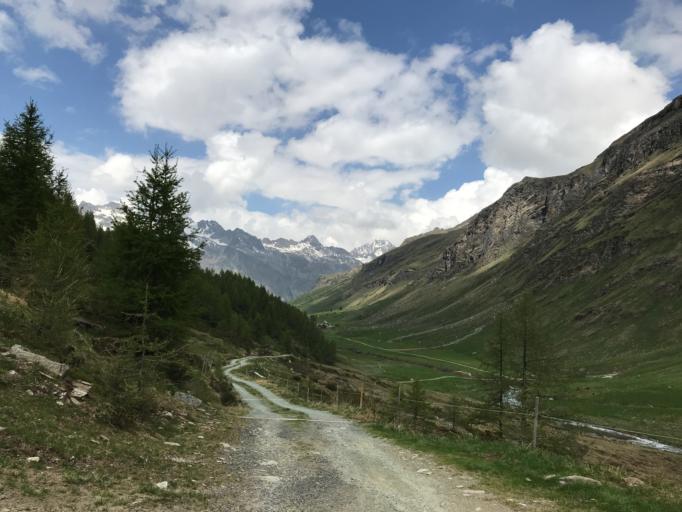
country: CH
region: Grisons
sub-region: Maloja District
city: Silvaplana
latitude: 46.3867
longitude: 9.7813
